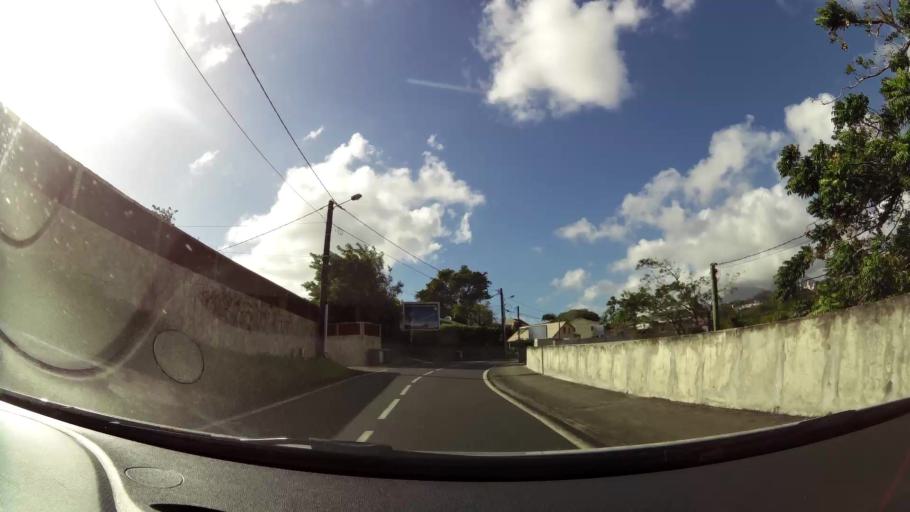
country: MQ
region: Martinique
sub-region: Martinique
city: Fort-de-France
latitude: 14.6414
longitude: -61.0755
